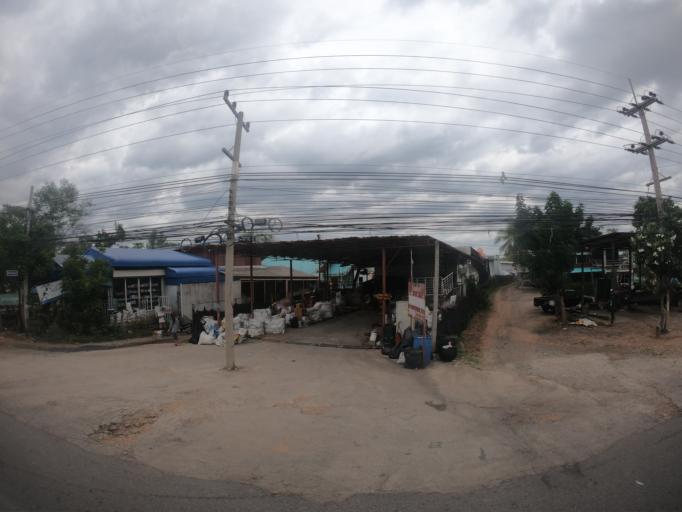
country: TH
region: Nakhon Ratchasima
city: Nakhon Ratchasima
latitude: 14.9014
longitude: 102.1590
